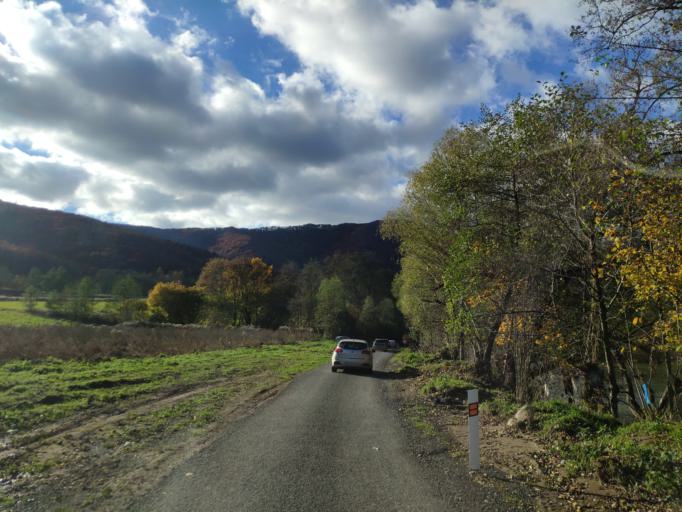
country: SK
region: Presovsky
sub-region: Okres Presov
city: Presov
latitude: 48.8536
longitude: 21.1720
